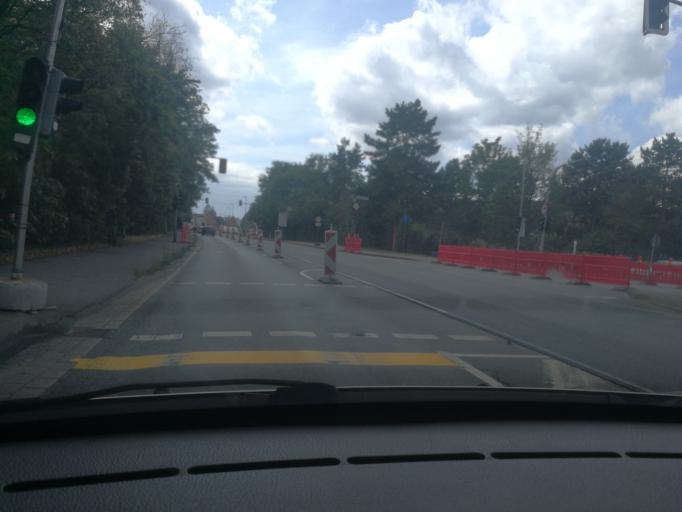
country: DE
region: North Rhine-Westphalia
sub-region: Regierungsbezirk Dusseldorf
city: Hochfeld
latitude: 51.3604
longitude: 6.6898
